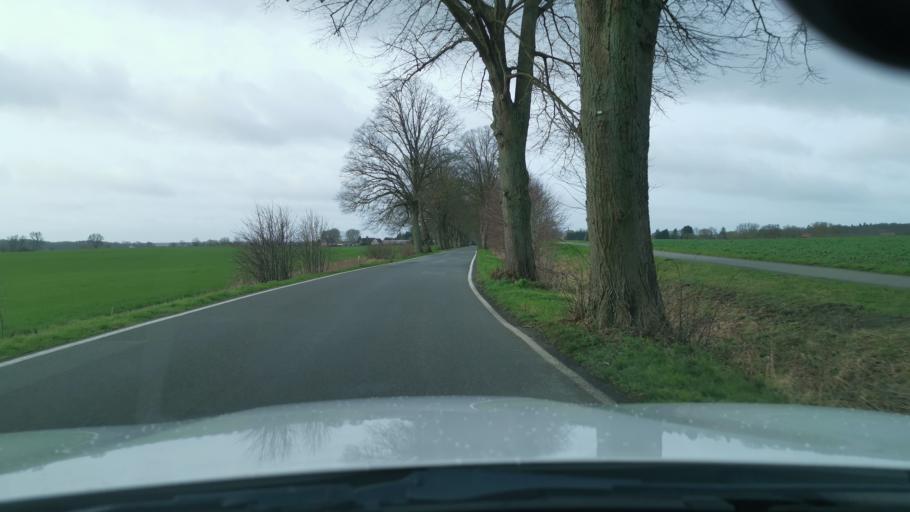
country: DE
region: Mecklenburg-Vorpommern
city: Wardow
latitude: 53.9940
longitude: 12.3741
